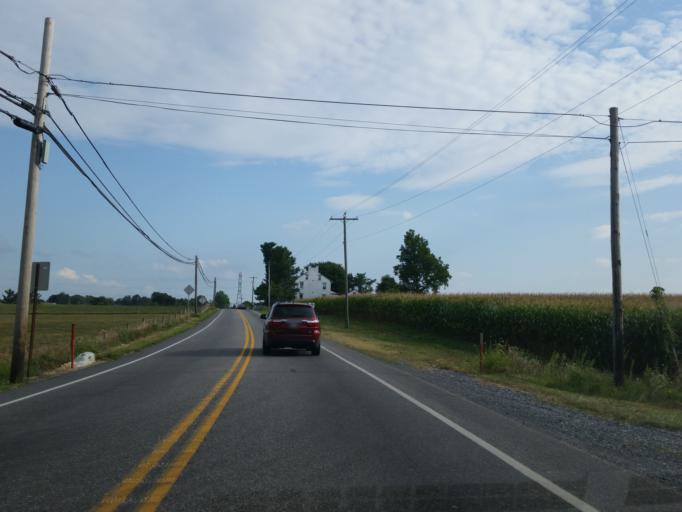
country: US
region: Pennsylvania
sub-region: Lebanon County
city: Annville
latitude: 40.3587
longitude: -76.5475
